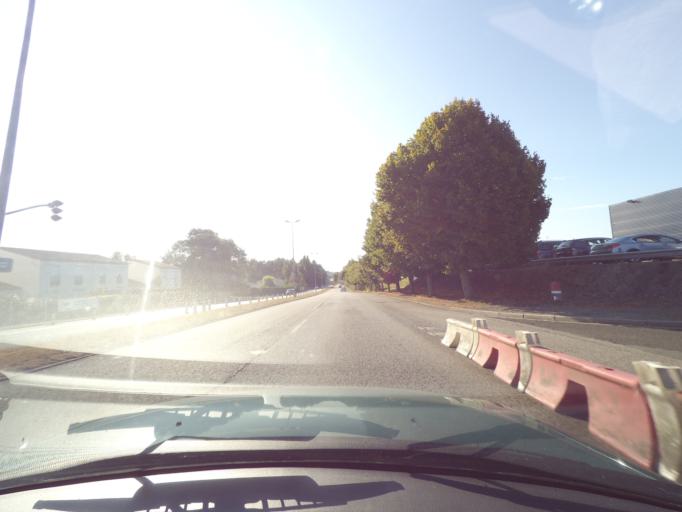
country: FR
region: Poitou-Charentes
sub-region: Departement des Deux-Sevres
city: Chatillon-sur-Thouet
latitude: 46.6524
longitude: -0.2287
